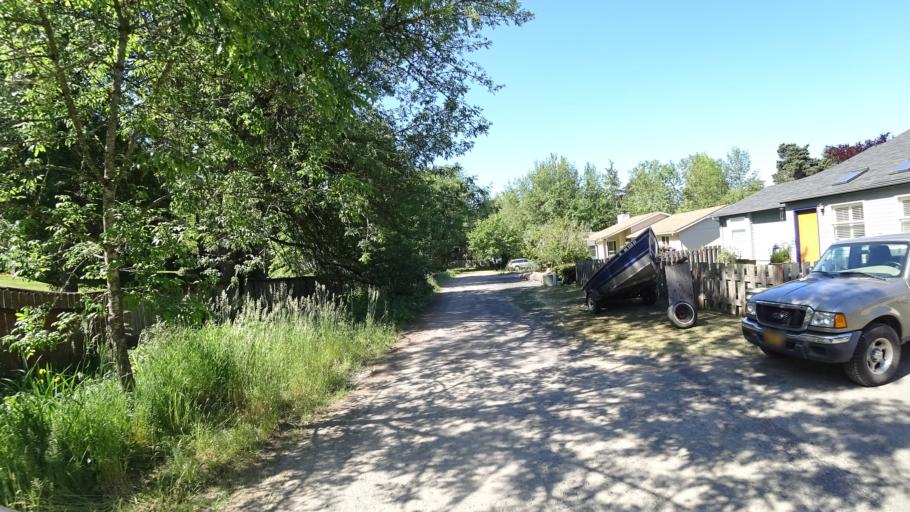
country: US
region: Oregon
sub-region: Washington County
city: Raleigh Hills
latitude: 45.4827
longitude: -122.7288
